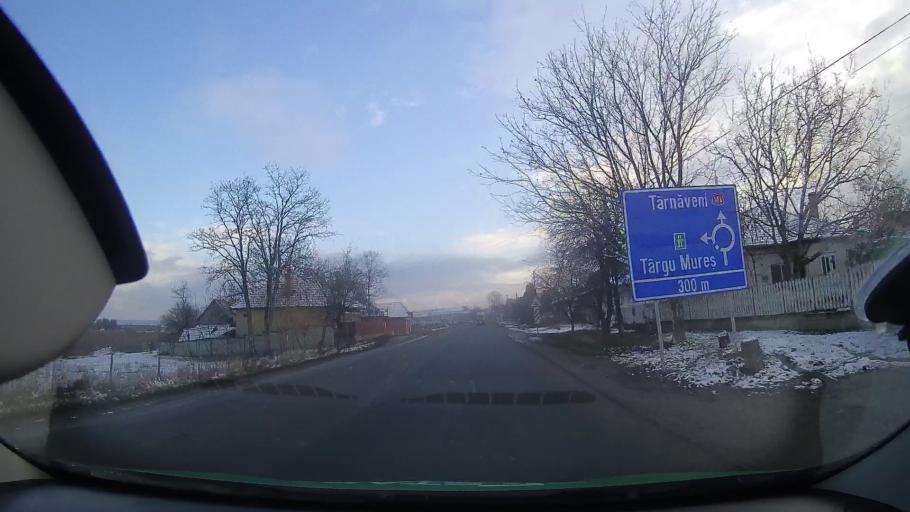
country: RO
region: Mures
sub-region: Comuna Iernut
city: Iernut
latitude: 46.4328
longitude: 24.2554
